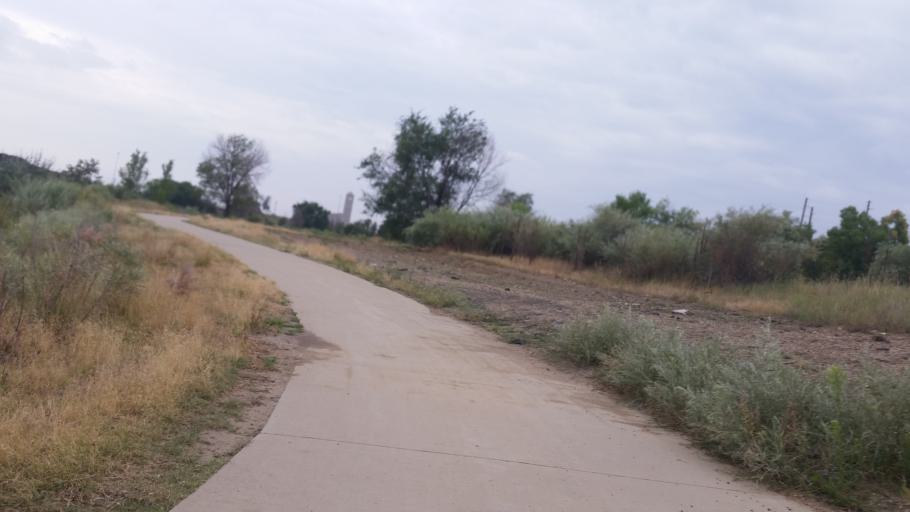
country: US
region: Colorado
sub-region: Adams County
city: Berkley
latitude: 39.8119
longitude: -105.0159
